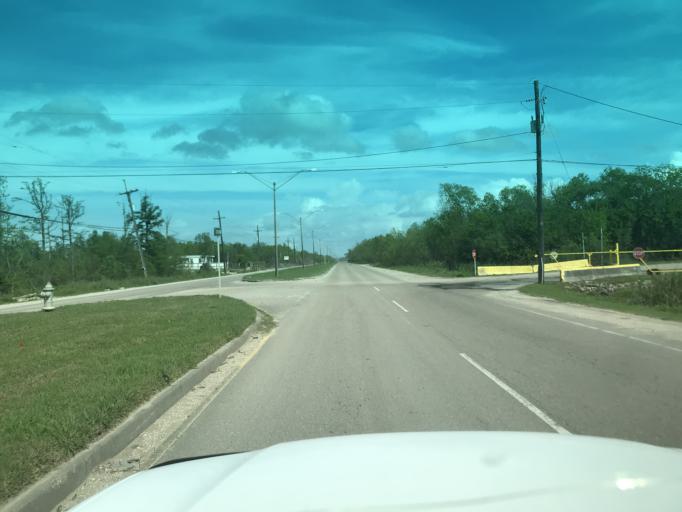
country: US
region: Louisiana
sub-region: Saint Bernard Parish
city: Arabi
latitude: 30.0095
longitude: -89.9766
